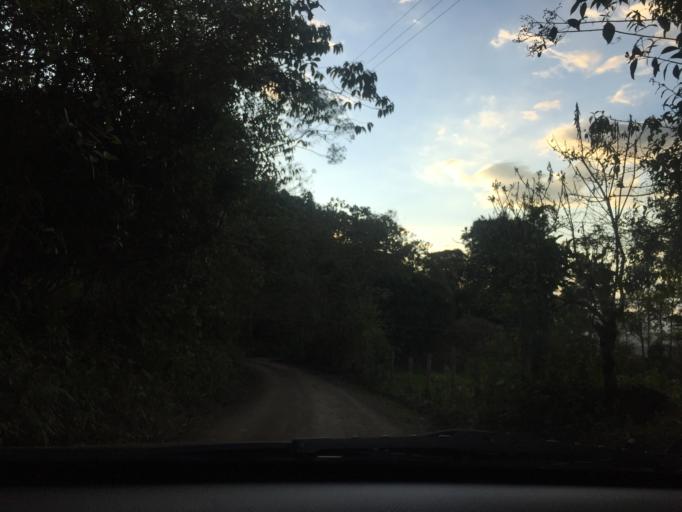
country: CO
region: Cundinamarca
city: Zipacon
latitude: 4.7085
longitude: -74.3997
